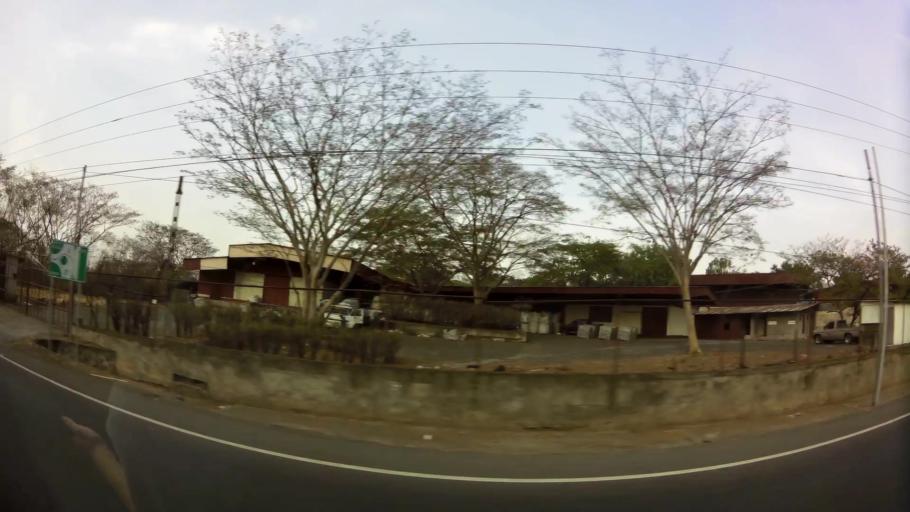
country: NI
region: Managua
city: Ciudad Sandino
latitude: 12.1432
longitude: -86.3347
